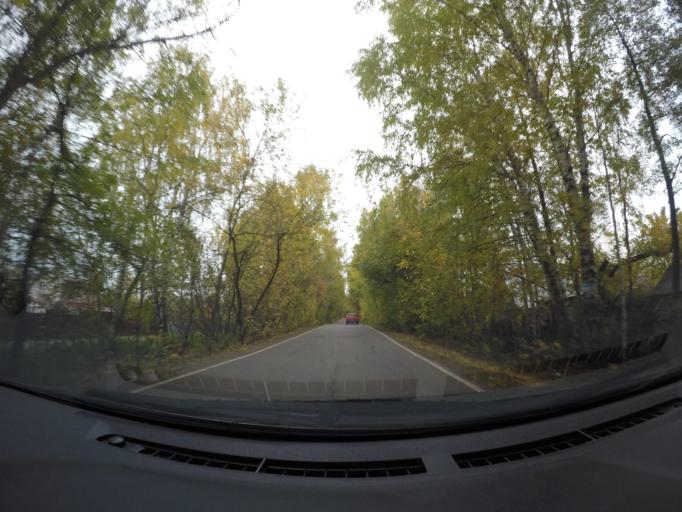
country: RU
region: Moskovskaya
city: Imeni Vorovskogo
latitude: 55.7309
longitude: 38.3010
